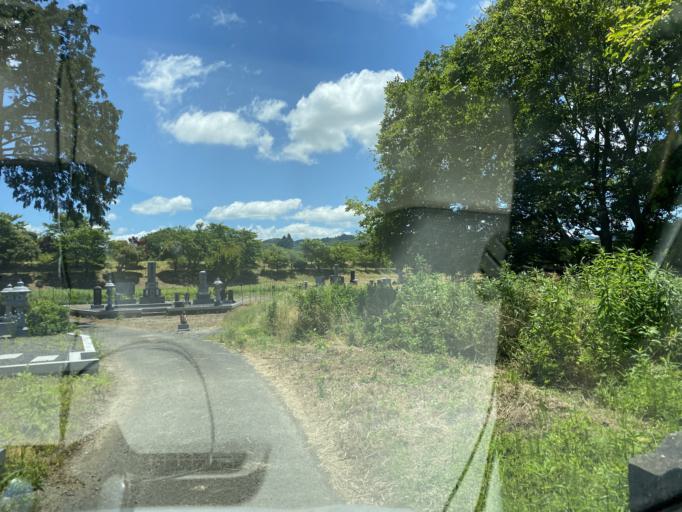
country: JP
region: Hyogo
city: Toyooka
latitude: 35.4896
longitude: 134.8080
